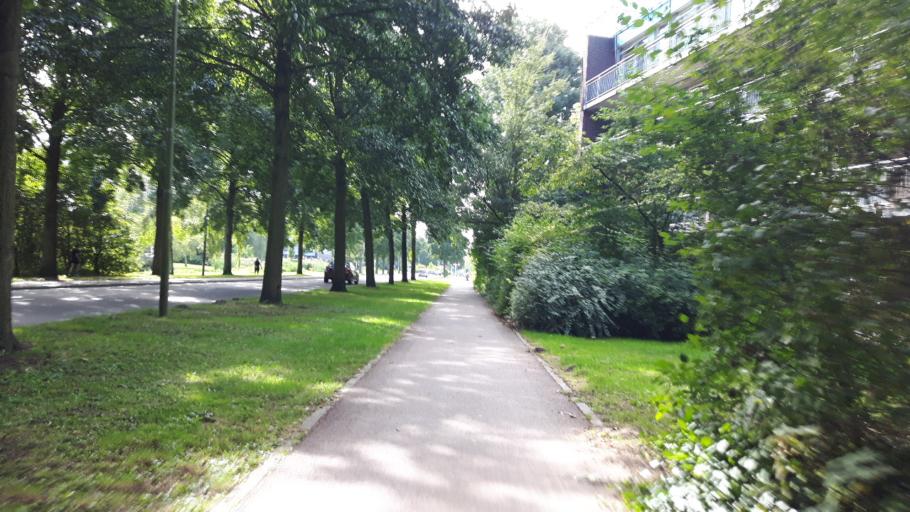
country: NL
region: North Holland
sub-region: Gemeente Purmerend
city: Purmerend
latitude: 52.5143
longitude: 4.9567
